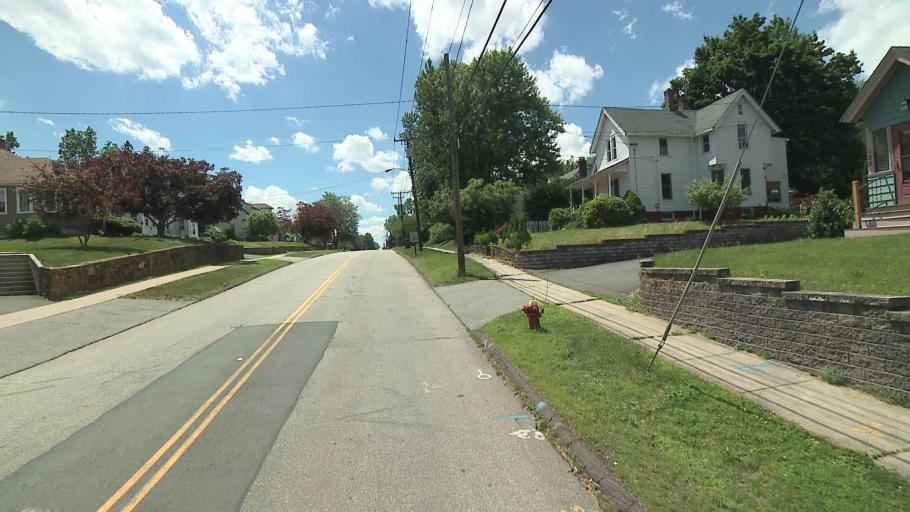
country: US
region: Connecticut
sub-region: Hartford County
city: Wethersfield
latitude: 41.7167
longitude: -72.6658
